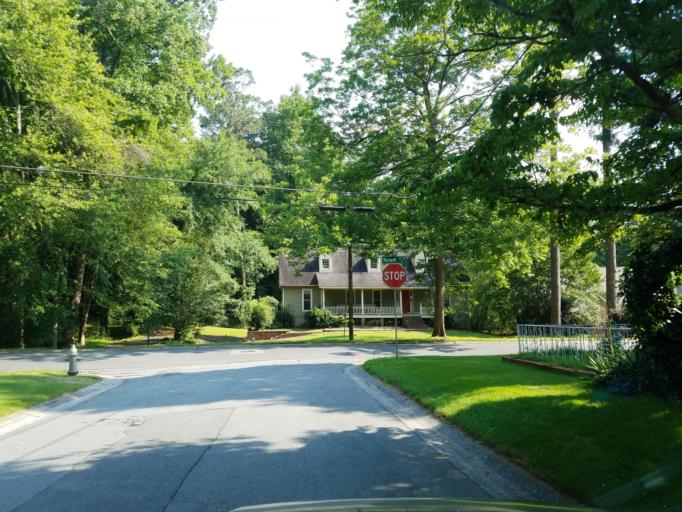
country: US
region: Georgia
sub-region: Cobb County
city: Marietta
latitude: 33.9498
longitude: -84.5633
